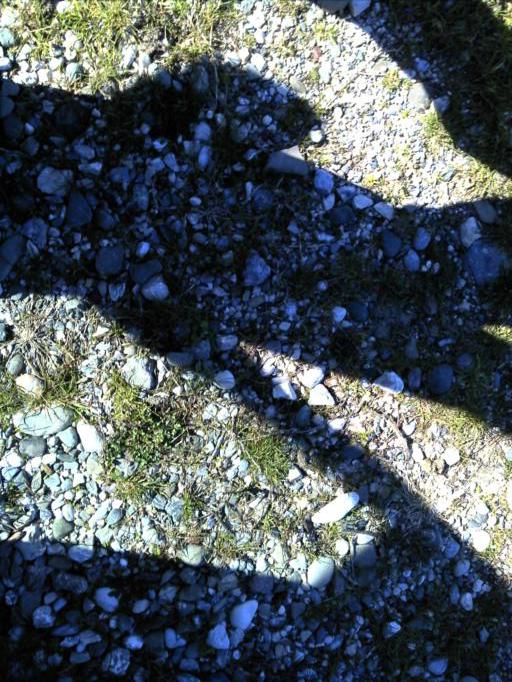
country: AL
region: Shkoder
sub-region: Rrethi i Shkodres
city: Velipoje
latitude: 41.9290
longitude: 19.4402
